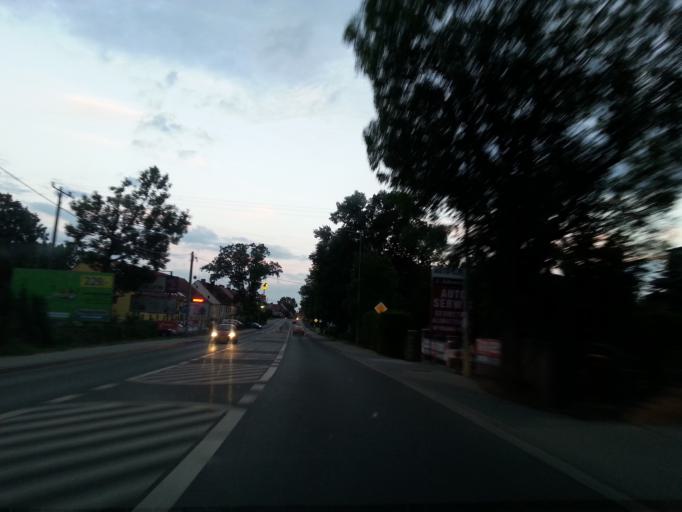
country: PL
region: Lower Silesian Voivodeship
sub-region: Powiat wroclawski
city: Bielany Wroclawskie
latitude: 51.0431
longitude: 16.9696
